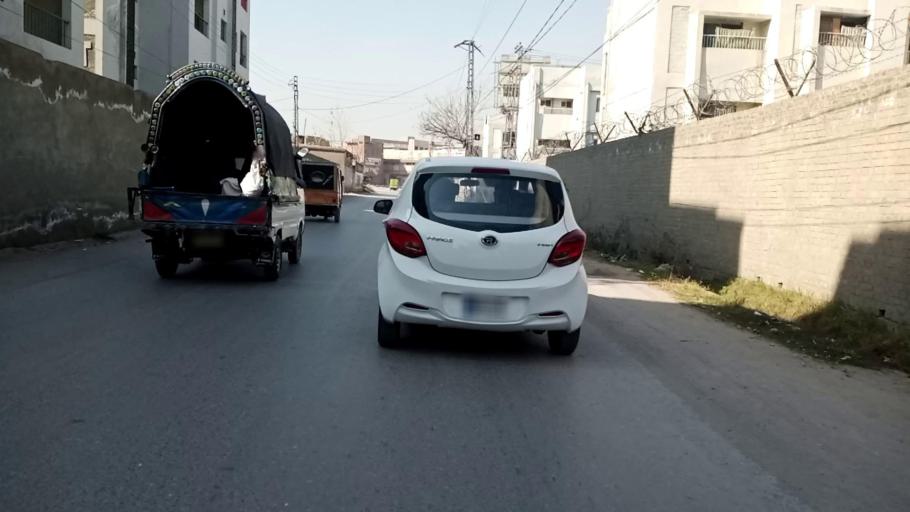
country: PK
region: Khyber Pakhtunkhwa
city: Peshawar
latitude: 33.9824
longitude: 71.5281
